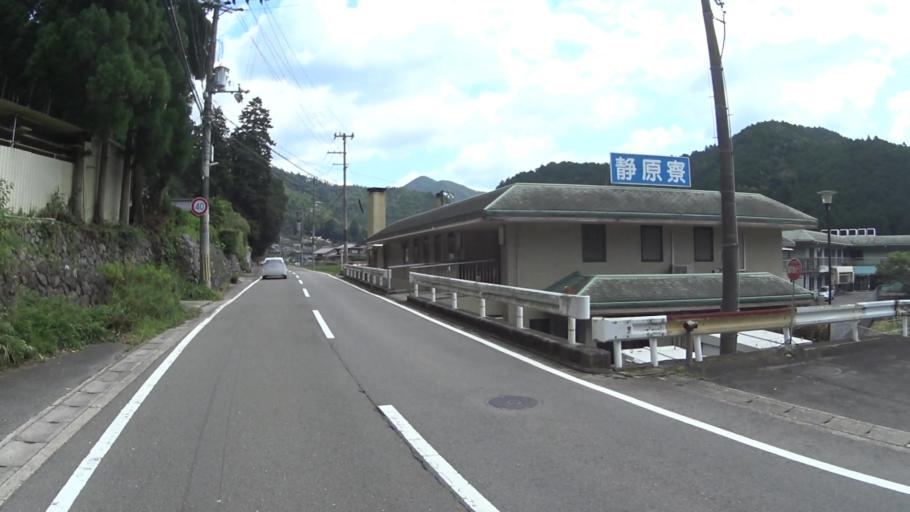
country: JP
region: Kyoto
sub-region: Kyoto-shi
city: Kamigyo-ku
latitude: 35.1071
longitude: 135.7827
